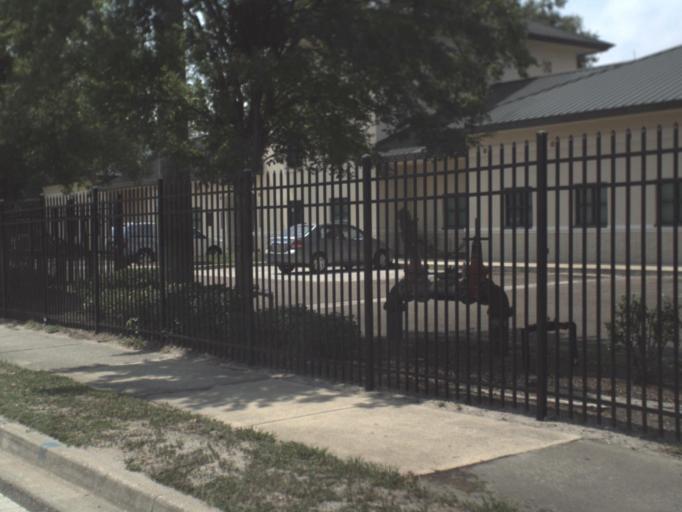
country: US
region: Florida
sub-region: Duval County
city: Jacksonville
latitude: 30.3575
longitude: -81.6398
